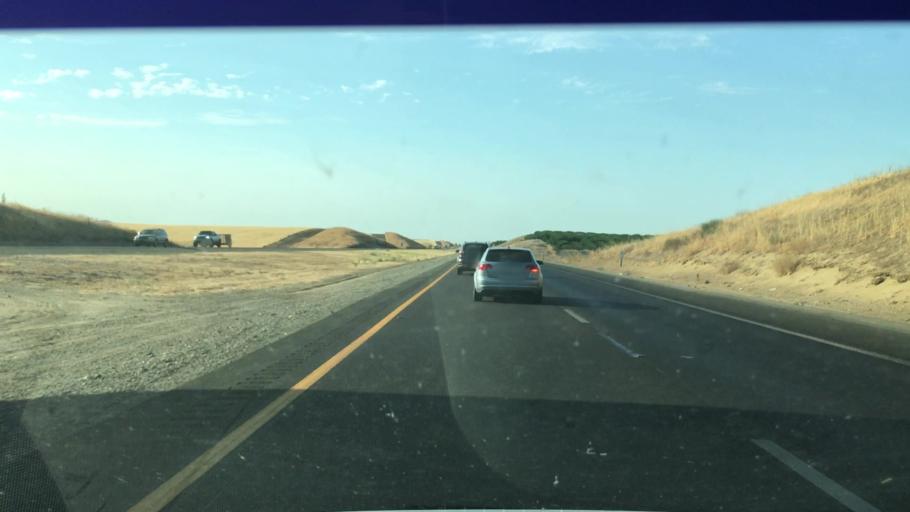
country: US
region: California
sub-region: Stanislaus County
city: Newman
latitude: 37.3528
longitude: -121.1188
